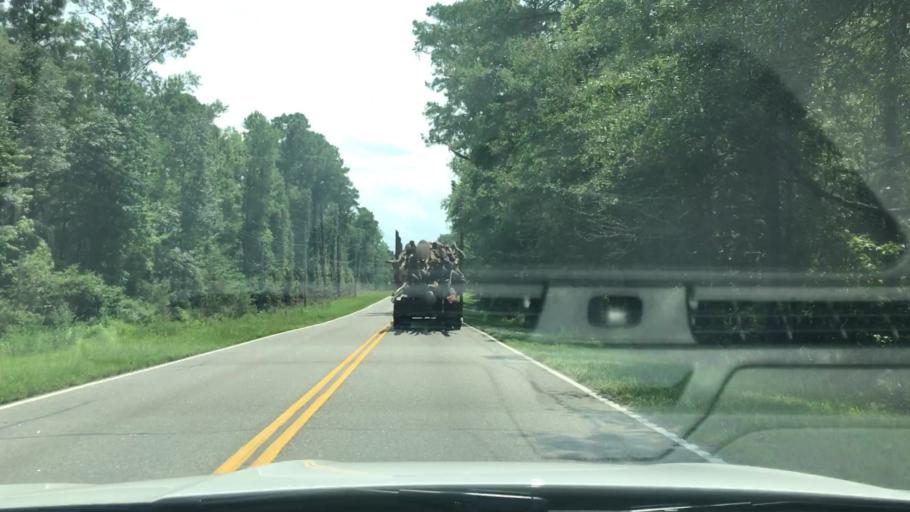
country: US
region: South Carolina
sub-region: Georgetown County
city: Georgetown
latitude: 33.4620
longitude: -79.2808
